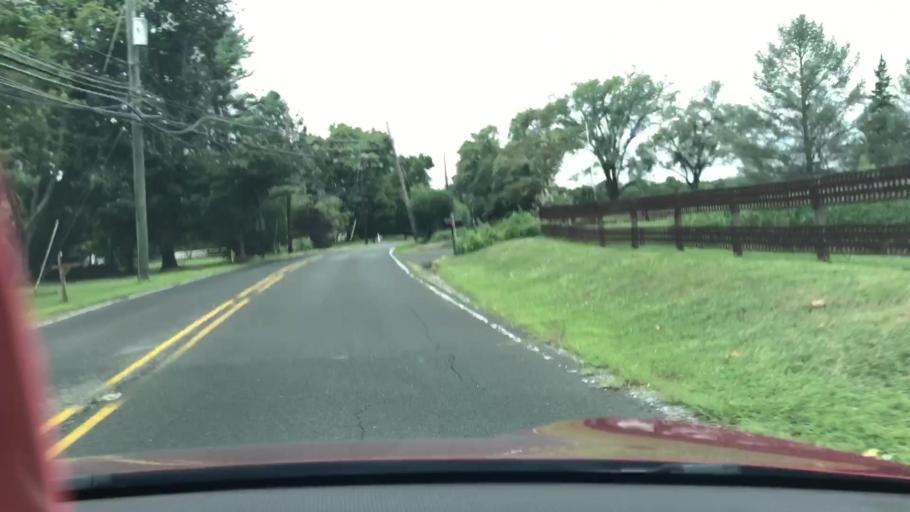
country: US
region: New Jersey
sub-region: Monmouth County
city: Allentown
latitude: 40.1840
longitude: -74.5921
